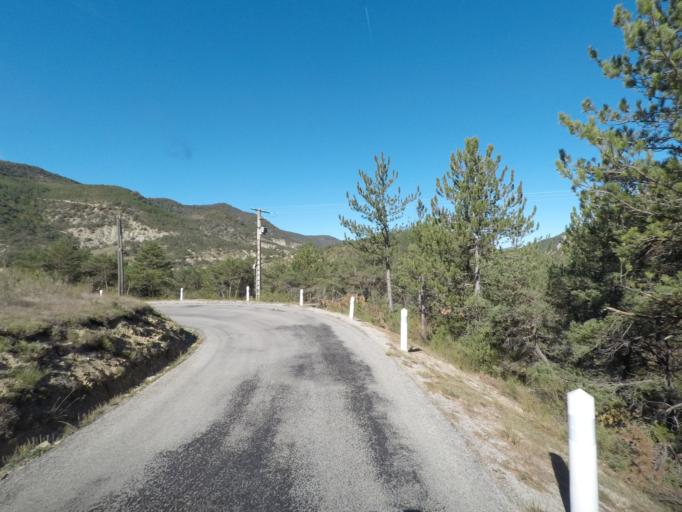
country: FR
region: Rhone-Alpes
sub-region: Departement de la Drome
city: Die
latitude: 44.5589
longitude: 5.3285
